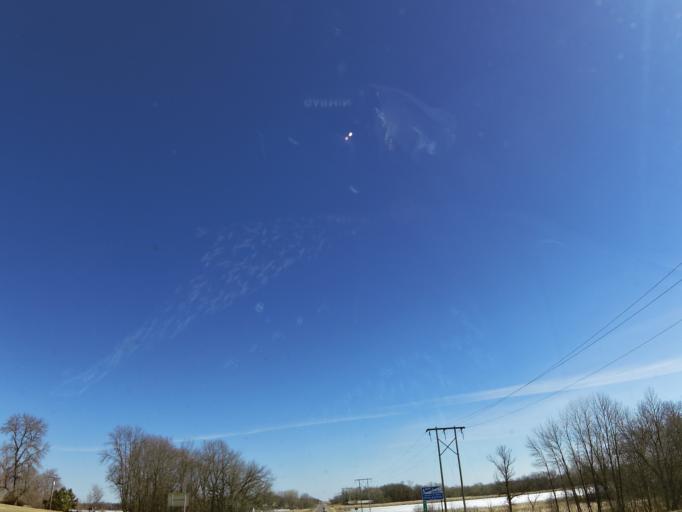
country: US
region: Minnesota
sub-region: Wright County
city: Maple Lake
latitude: 45.2274
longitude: -93.9845
